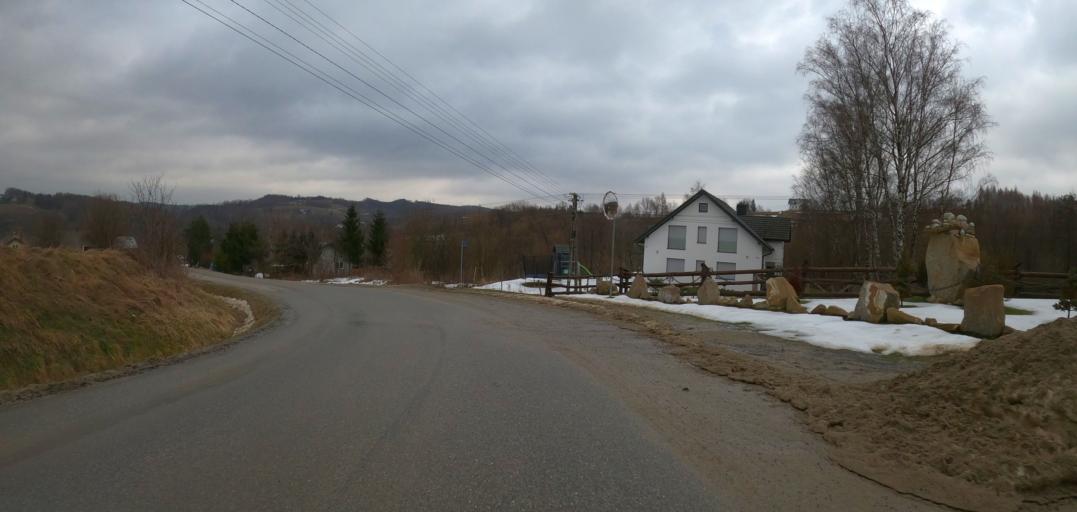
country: PL
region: Subcarpathian Voivodeship
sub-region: Powiat debicki
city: Debica
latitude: 49.9922
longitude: 21.4276
